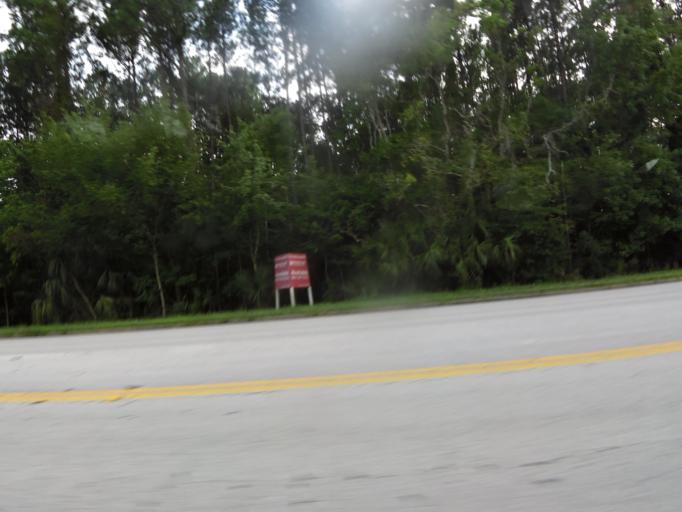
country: US
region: Florida
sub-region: Duval County
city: Jacksonville
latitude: 30.3389
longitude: -81.7711
